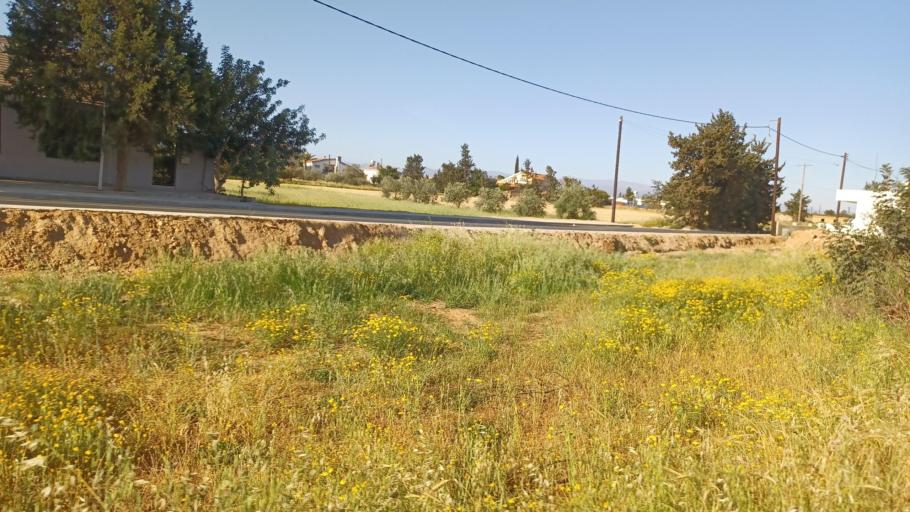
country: CY
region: Lefkosia
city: Kokkinotrimithia
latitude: 35.1489
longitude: 33.1899
